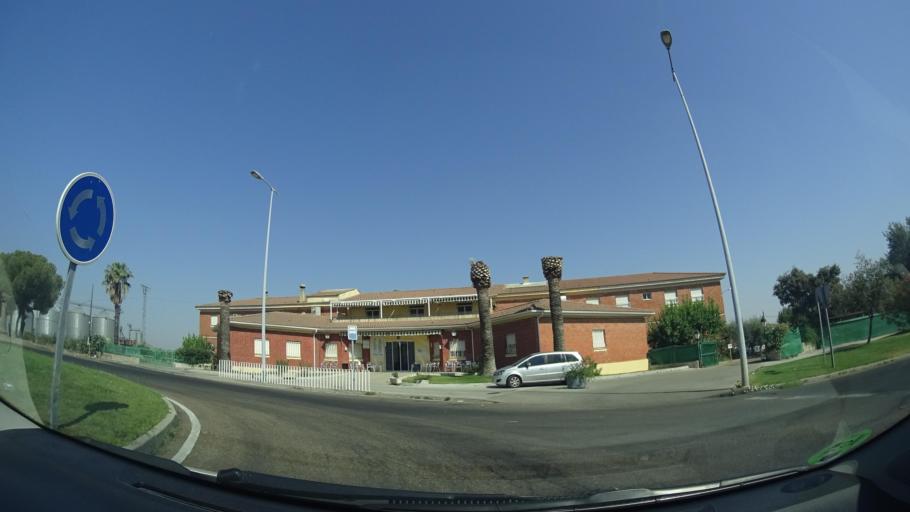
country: ES
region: Extremadura
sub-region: Provincia de Caceres
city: Miajadas
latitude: 39.1437
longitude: -5.9250
